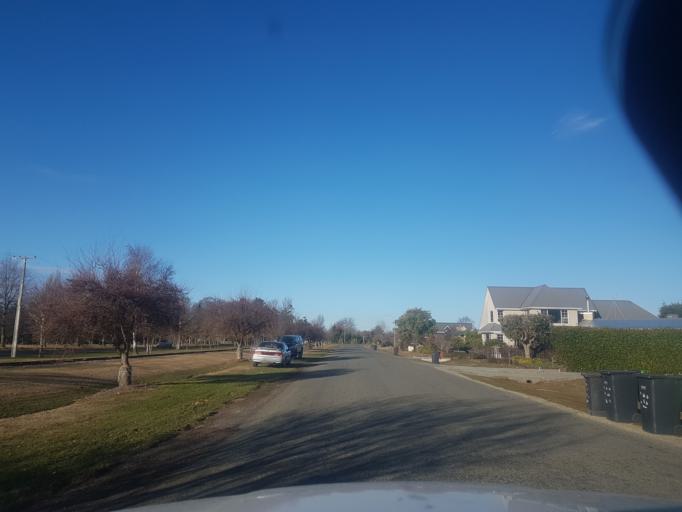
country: NZ
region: Canterbury
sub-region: Timaru District
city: Pleasant Point
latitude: -44.2638
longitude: 171.1389
